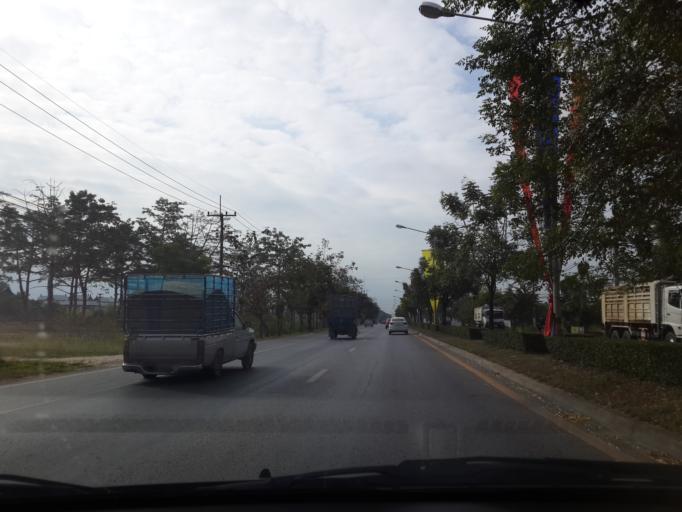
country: TH
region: Chiang Mai
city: San Sai
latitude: 18.8523
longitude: 99.0142
